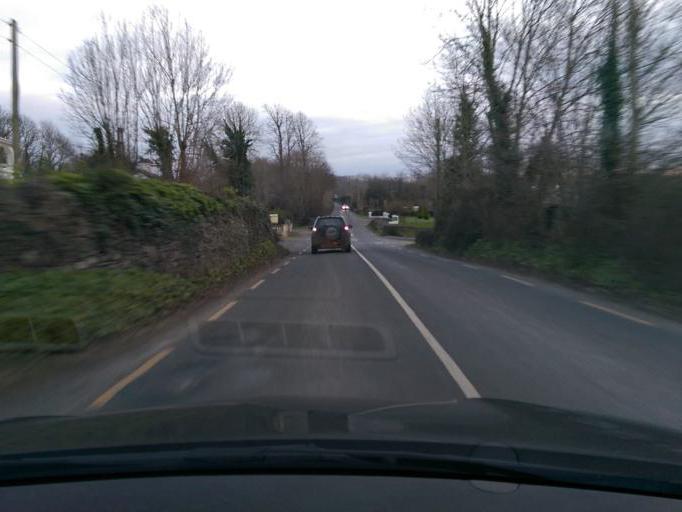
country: IE
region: Connaught
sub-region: County Galway
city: Portumna
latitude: 53.0953
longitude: -8.1829
